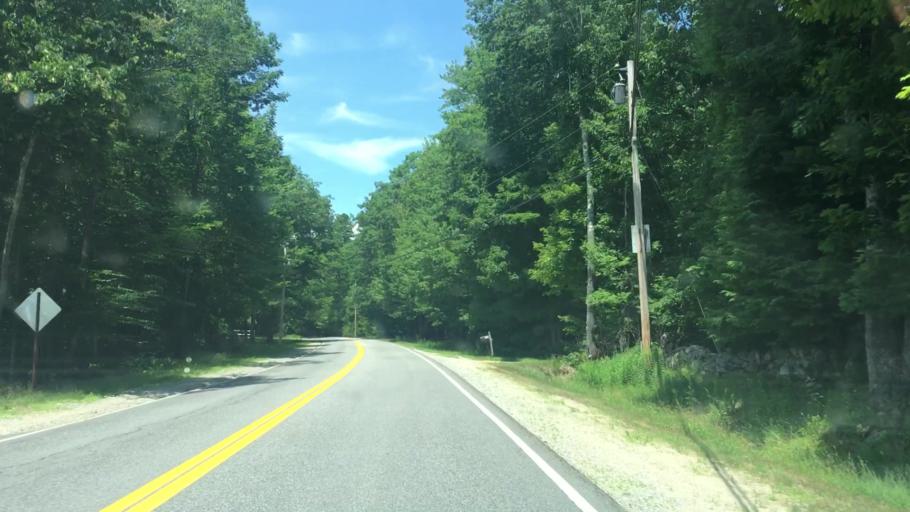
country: US
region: Maine
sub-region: Androscoggin County
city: Livermore
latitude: 44.3860
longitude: -70.2142
